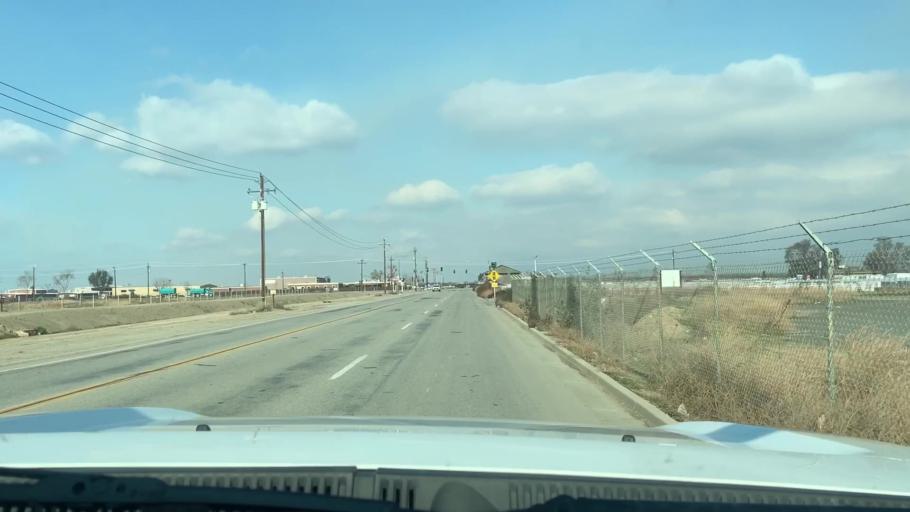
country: US
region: California
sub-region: Kern County
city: Shafter
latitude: 35.4974
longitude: -119.1702
